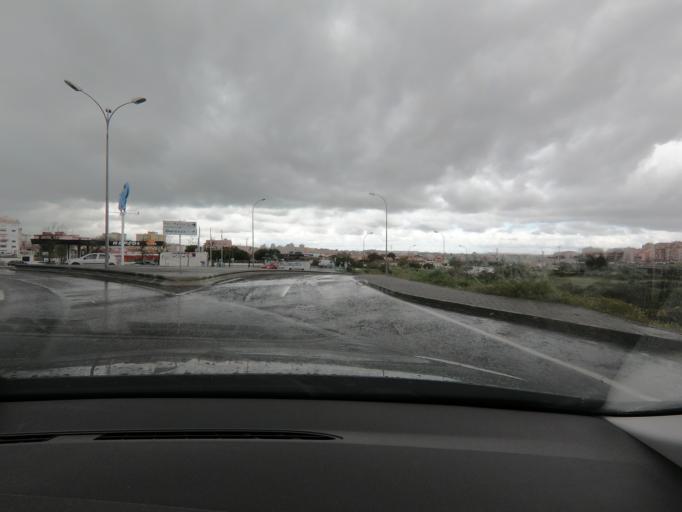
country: PT
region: Lisbon
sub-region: Sintra
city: Sintra
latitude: 38.8032
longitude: -9.3573
